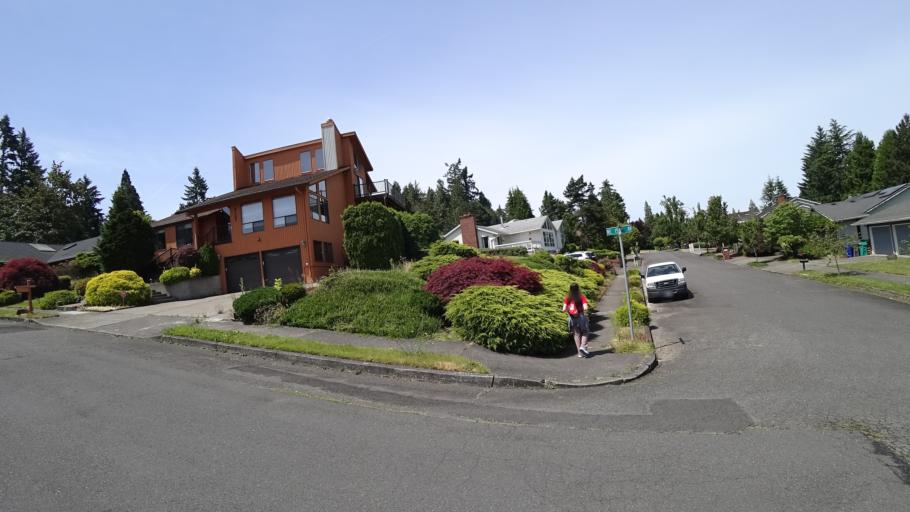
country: US
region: Oregon
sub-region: Multnomah County
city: Fairview
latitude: 45.5458
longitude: -122.4996
